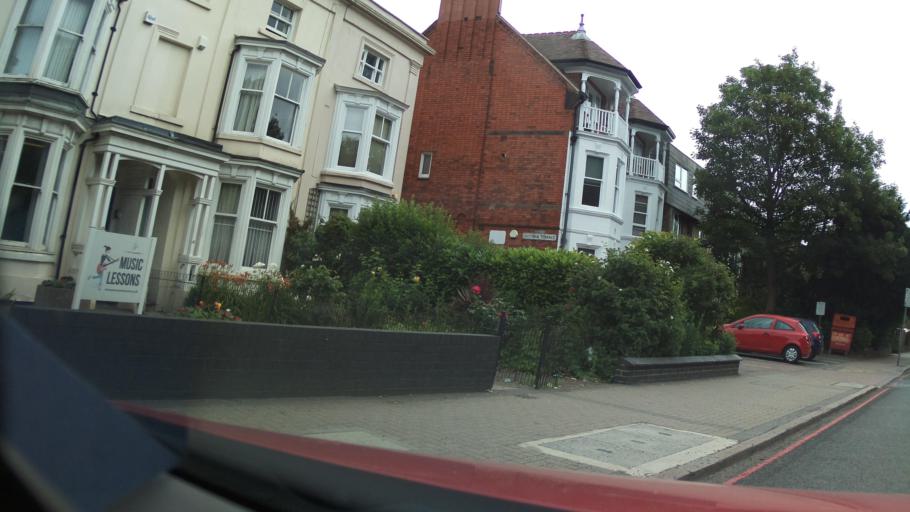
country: GB
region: England
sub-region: City of Leicester
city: Leicester
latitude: 52.6256
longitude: -1.1168
